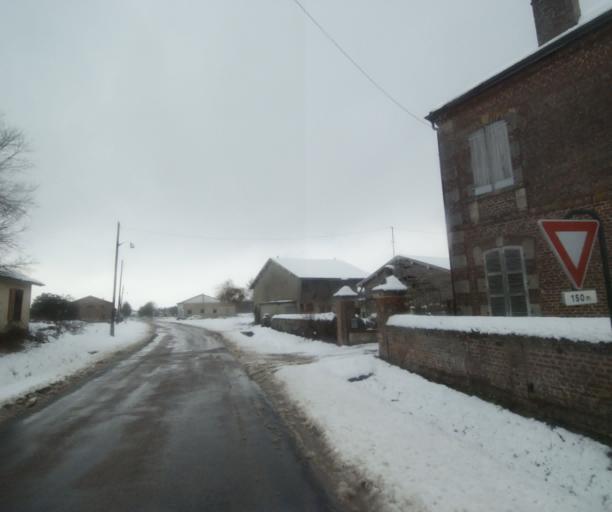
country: FR
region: Champagne-Ardenne
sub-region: Departement de la Haute-Marne
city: Montier-en-Der
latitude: 48.4731
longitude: 4.7866
